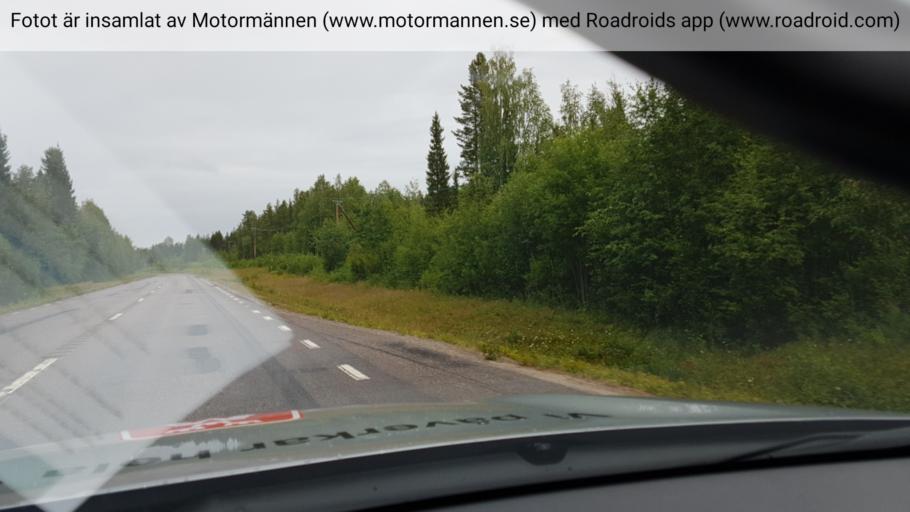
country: SE
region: Norrbotten
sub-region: Alvsbyns Kommun
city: AElvsbyn
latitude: 66.1615
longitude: 20.8800
